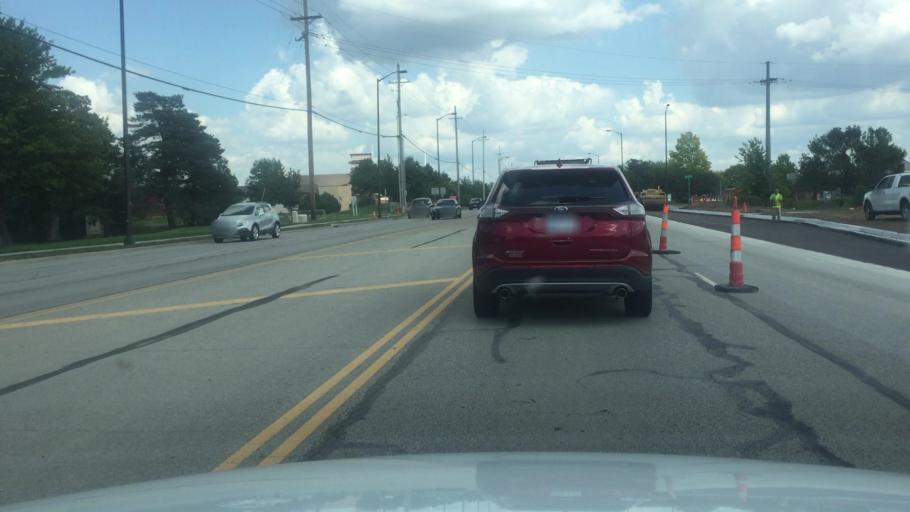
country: US
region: Kansas
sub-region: Johnson County
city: Lenexa
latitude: 38.9710
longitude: -94.7715
